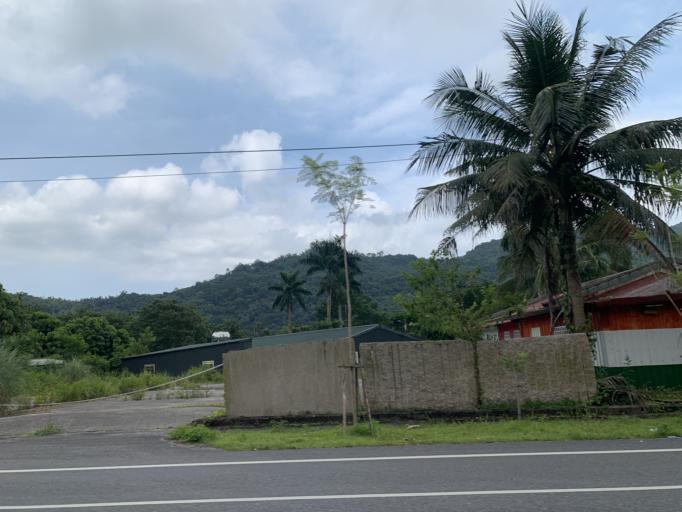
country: TW
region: Taiwan
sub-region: Hualien
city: Hualian
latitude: 23.9346
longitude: 121.5062
